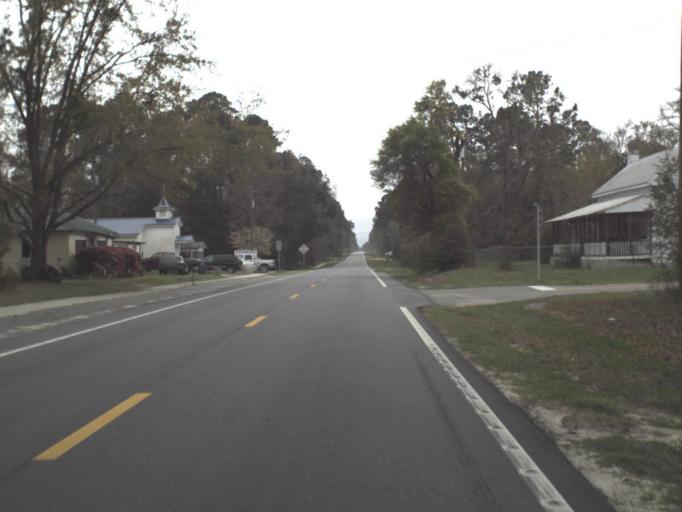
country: US
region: Florida
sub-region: Gulf County
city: Wewahitchka
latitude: 30.0198
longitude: -84.9796
